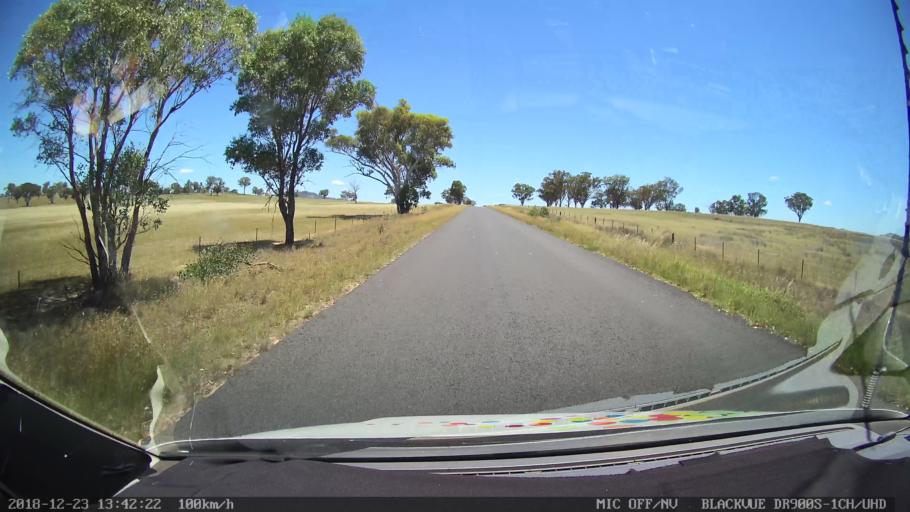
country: AU
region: New South Wales
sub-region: Armidale Dumaresq
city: Armidale
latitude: -30.4762
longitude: 151.1634
